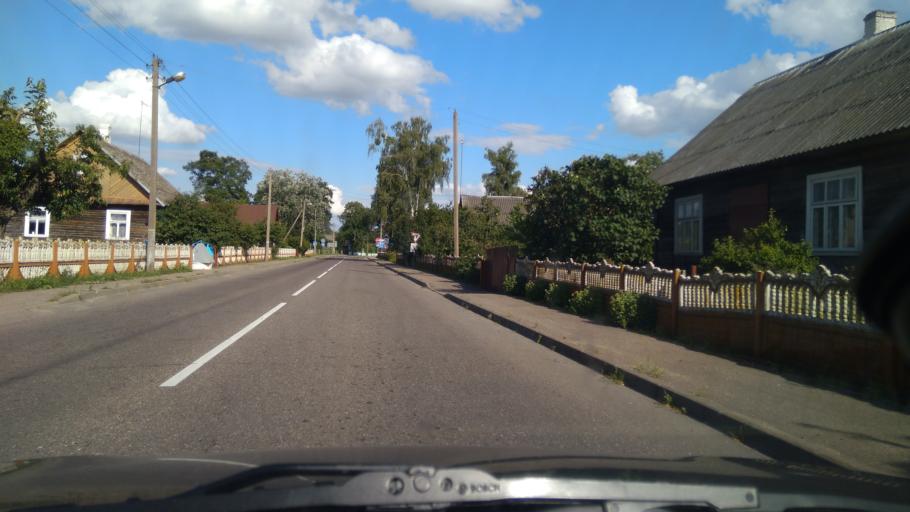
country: BY
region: Grodnenskaya
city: Masty
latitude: 53.3508
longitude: 24.6214
